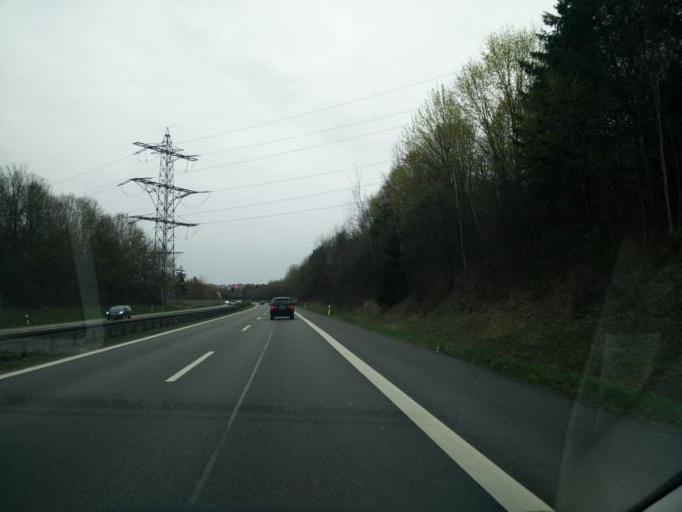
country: DE
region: Baden-Wuerttemberg
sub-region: Tuebingen Region
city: Pliezhausen
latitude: 48.5661
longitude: 9.1758
